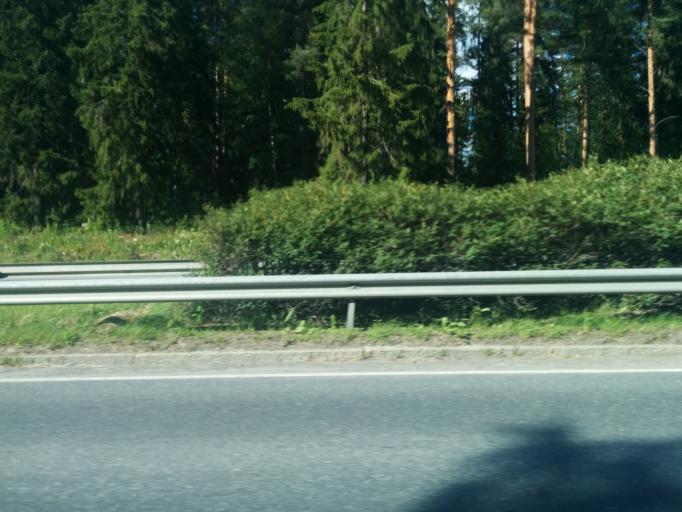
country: FI
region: Pirkanmaa
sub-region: Tampere
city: Tampere
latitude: 61.5012
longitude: 23.8703
